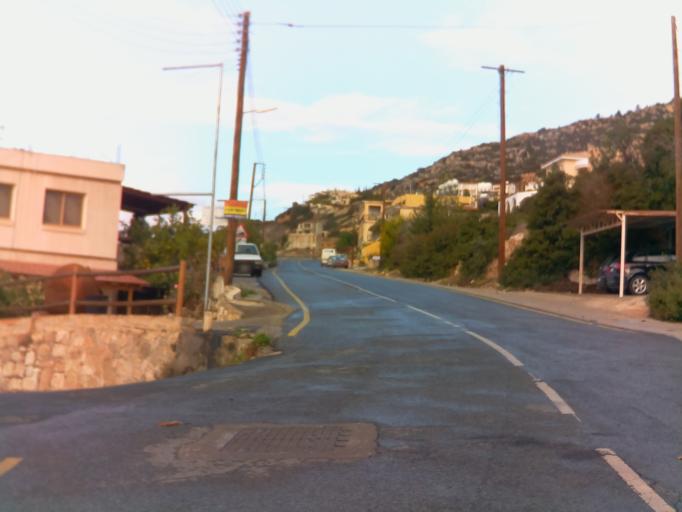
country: CY
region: Pafos
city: Pegeia
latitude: 34.8850
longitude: 32.3790
